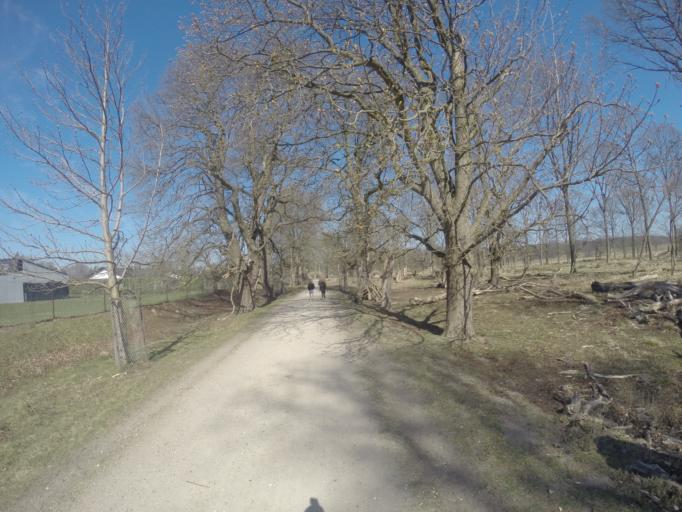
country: DK
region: Capital Region
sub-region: Rudersdal Kommune
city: Trorod
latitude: 55.7965
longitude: 12.5446
